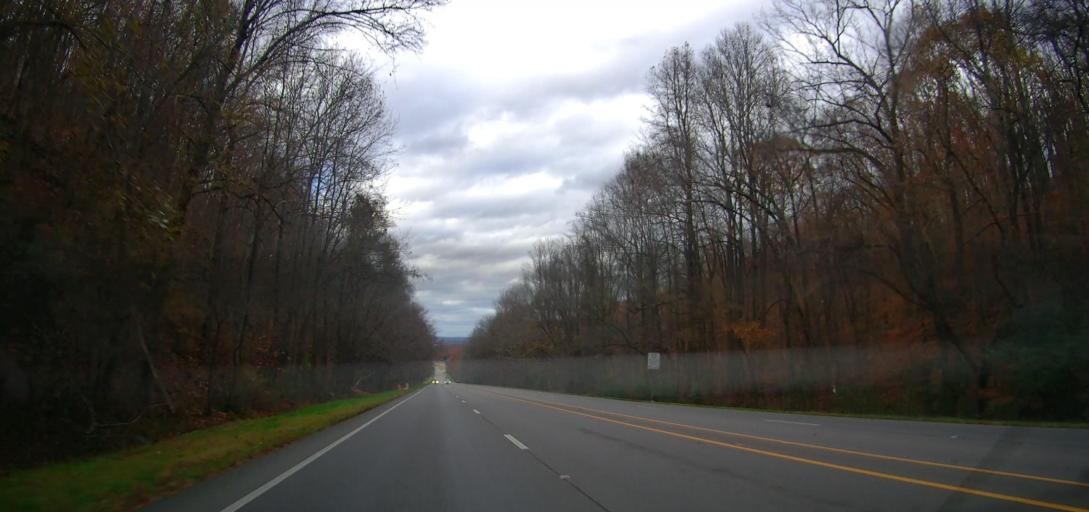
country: US
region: Alabama
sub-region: Morgan County
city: Falkville
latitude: 34.3111
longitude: -86.9981
